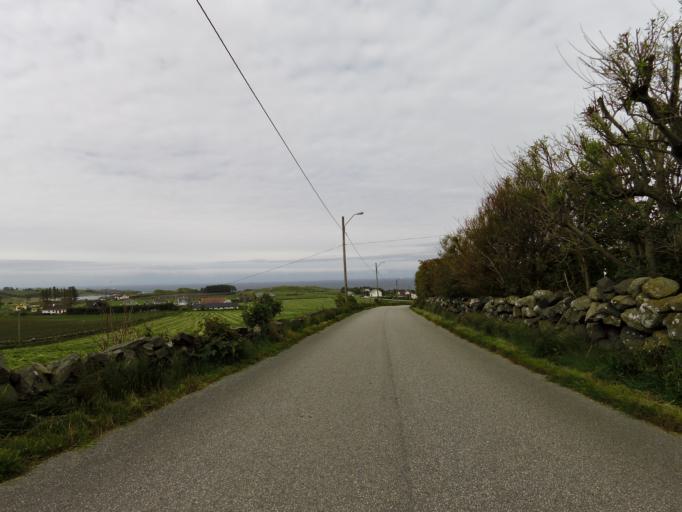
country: NO
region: Rogaland
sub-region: Sola
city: Tananger
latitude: 58.8653
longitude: 5.5751
